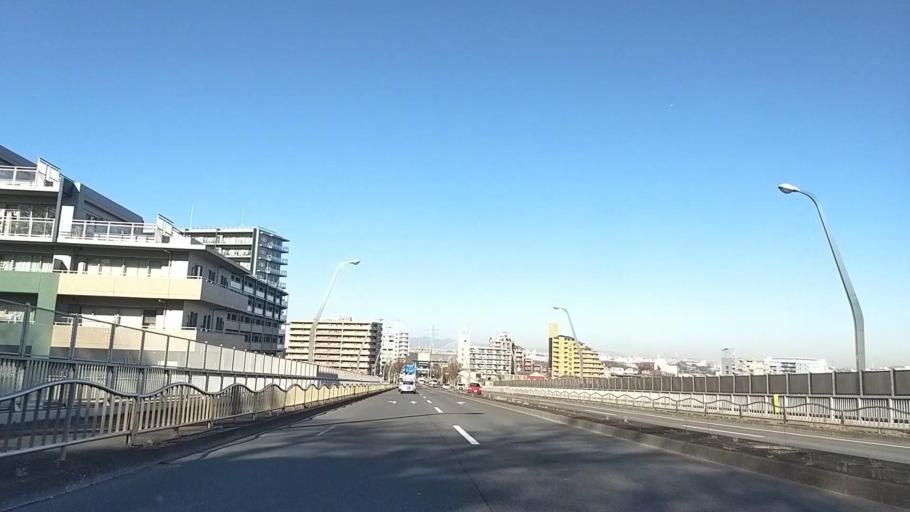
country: JP
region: Tokyo
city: Kokubunji
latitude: 35.6462
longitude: 139.4567
